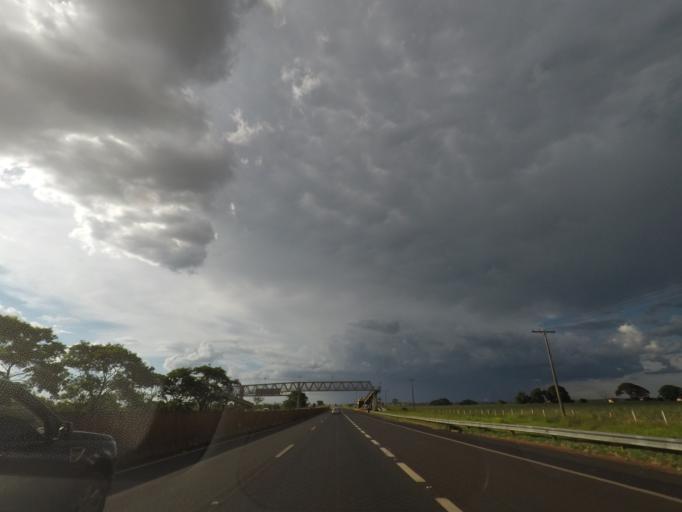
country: BR
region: Sao Paulo
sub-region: Jardinopolis
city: Jardinopolis
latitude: -21.0890
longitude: -47.7971
